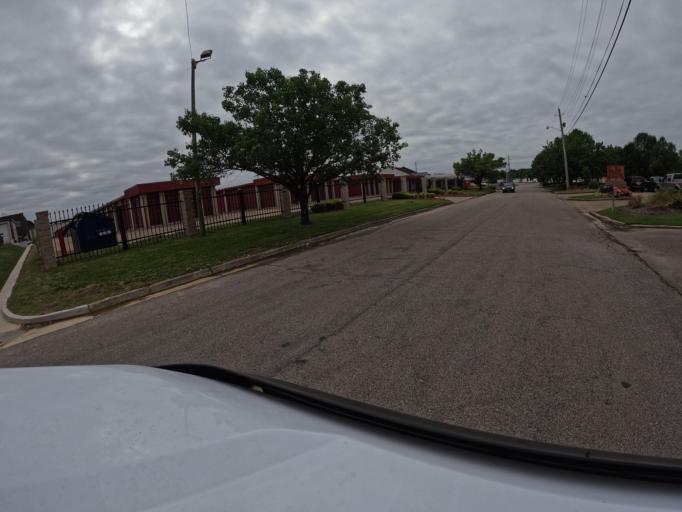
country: US
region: Mississippi
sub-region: Lee County
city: Tupelo
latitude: 34.2563
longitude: -88.7489
